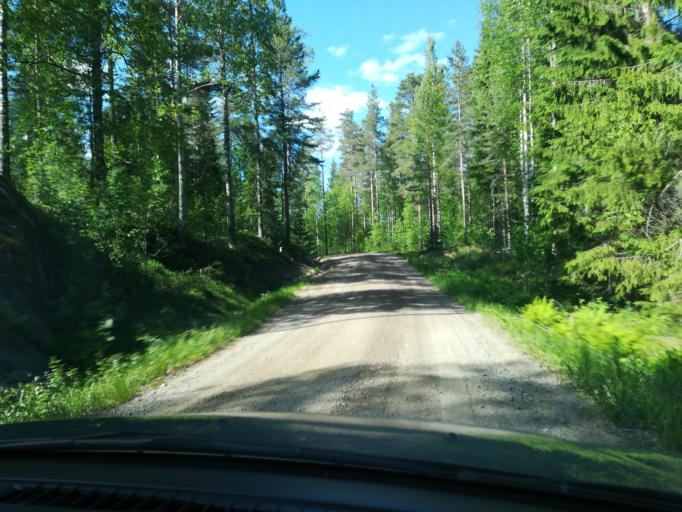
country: FI
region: Southern Savonia
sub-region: Mikkeli
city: Puumala
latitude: 61.6507
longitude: 28.1780
